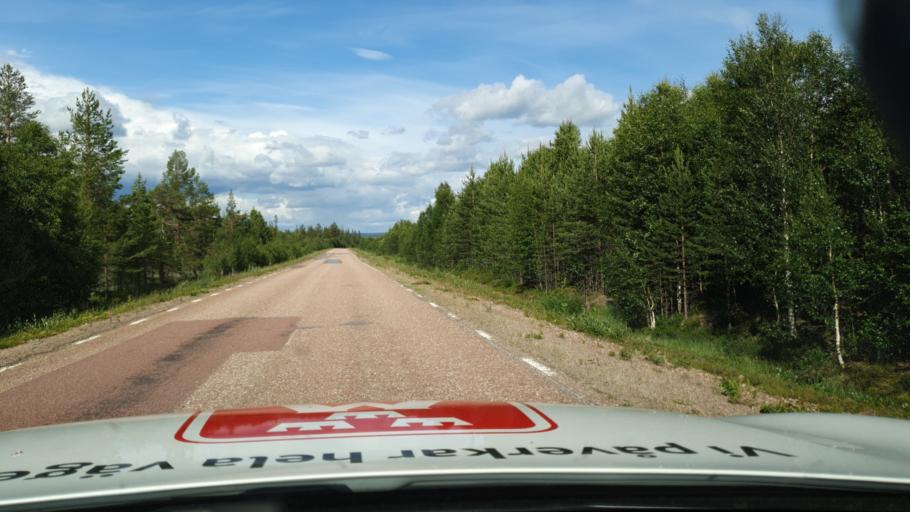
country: SE
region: Dalarna
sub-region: Alvdalens Kommun
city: AElvdalen
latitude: 61.7820
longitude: 13.4865
